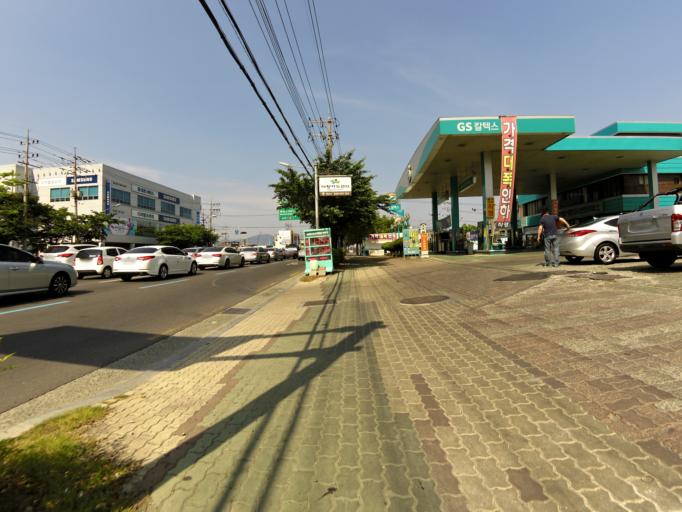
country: KR
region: Daegu
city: Daegu
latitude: 35.8759
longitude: 128.6441
